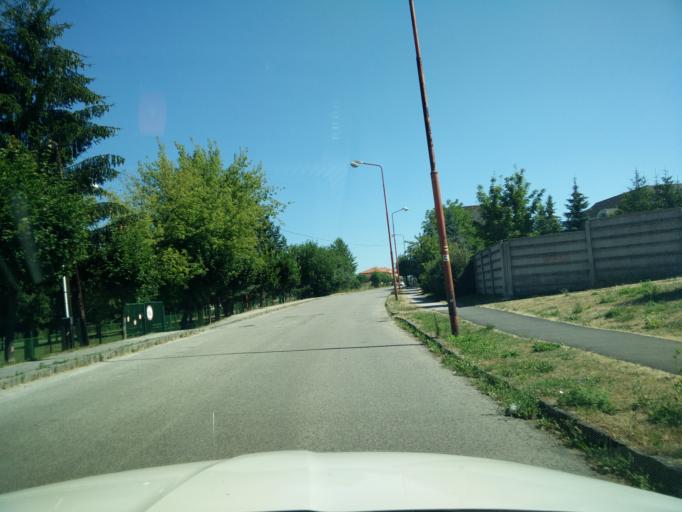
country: SK
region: Nitriansky
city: Prievidza
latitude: 48.8716
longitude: 18.6365
